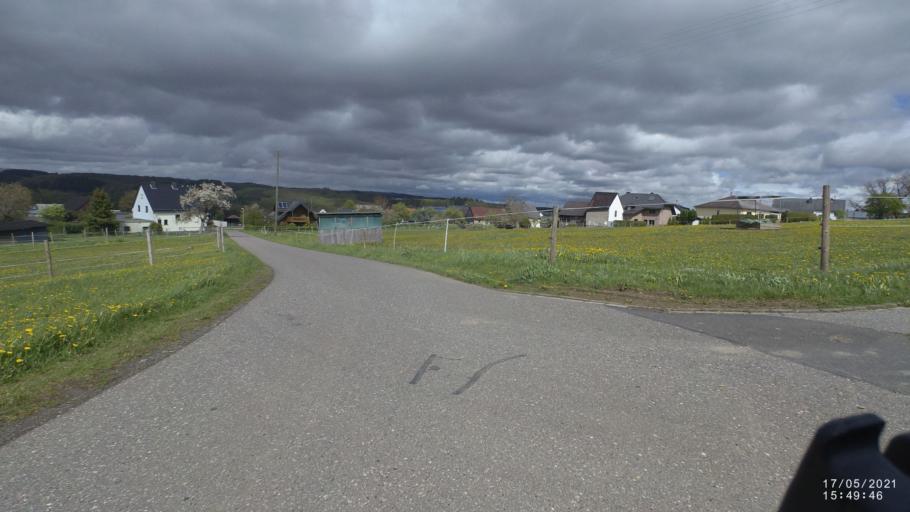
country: DE
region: Rheinland-Pfalz
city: Munk
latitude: 50.3055
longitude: 7.0381
